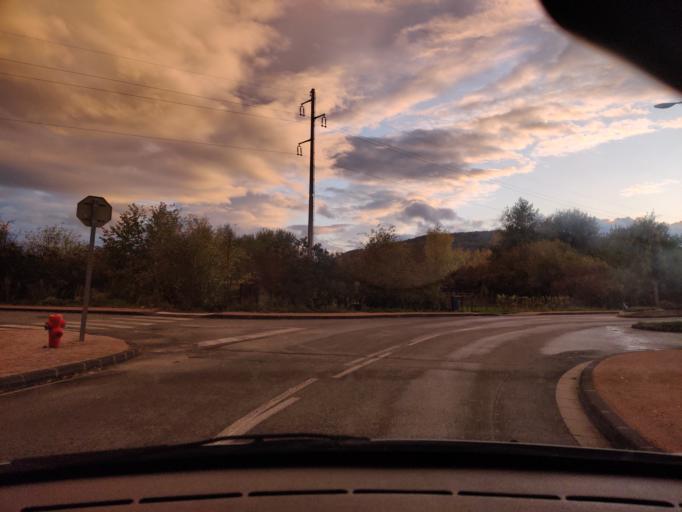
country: FR
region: Auvergne
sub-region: Departement du Puy-de-Dome
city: Menetrol
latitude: 45.8786
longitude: 3.1217
